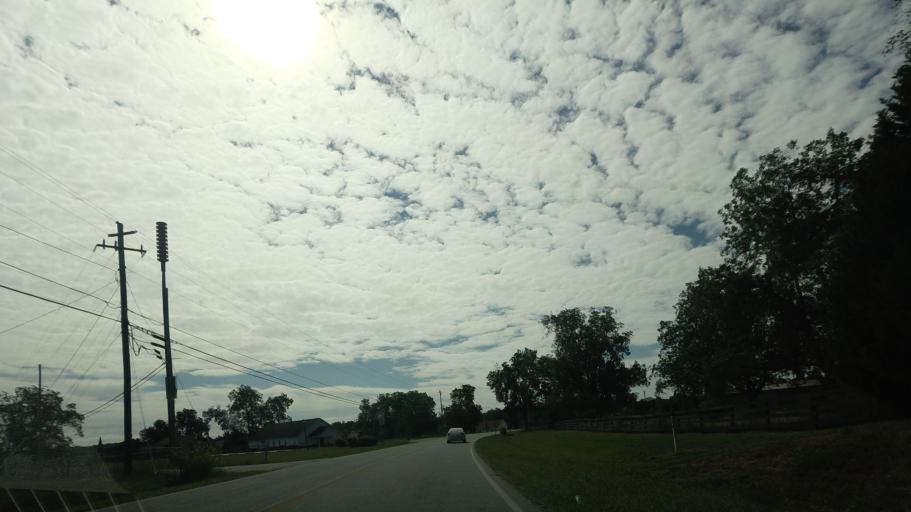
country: US
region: Georgia
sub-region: Houston County
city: Centerville
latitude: 32.6683
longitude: -83.6999
